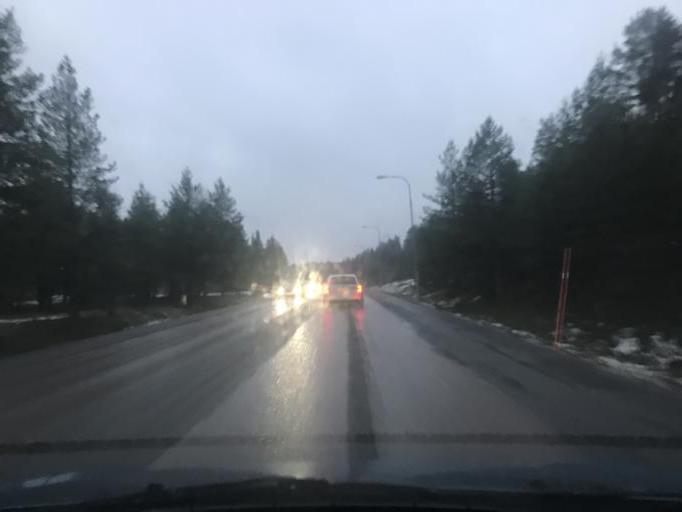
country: SE
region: Norrbotten
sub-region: Lulea Kommun
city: Gammelstad
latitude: 65.6236
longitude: 22.0356
